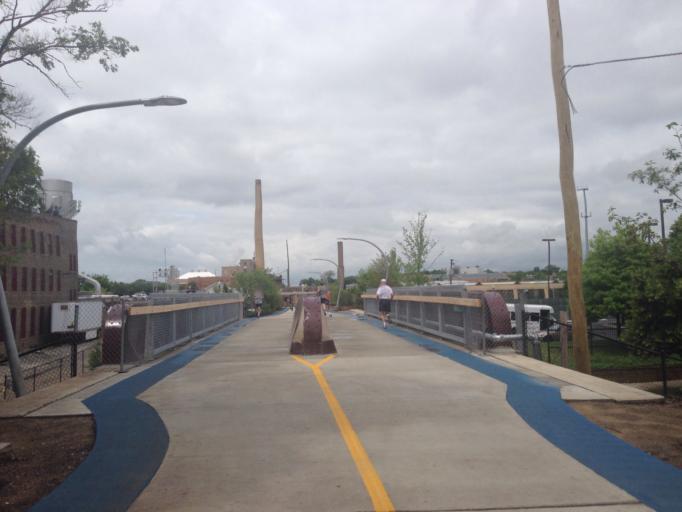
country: US
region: Illinois
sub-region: Cook County
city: Oak Park
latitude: 41.9137
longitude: -87.7188
